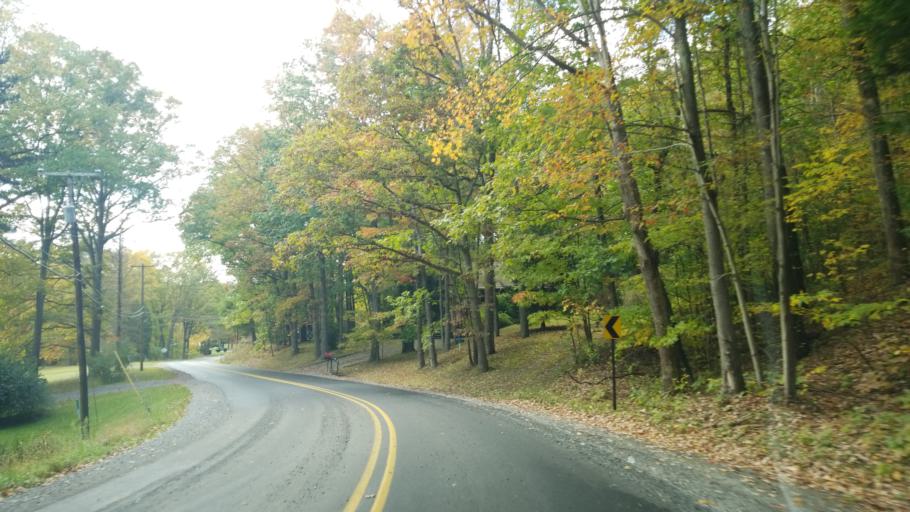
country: US
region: Pennsylvania
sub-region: Clearfield County
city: Sandy
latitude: 41.0921
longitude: -78.7855
